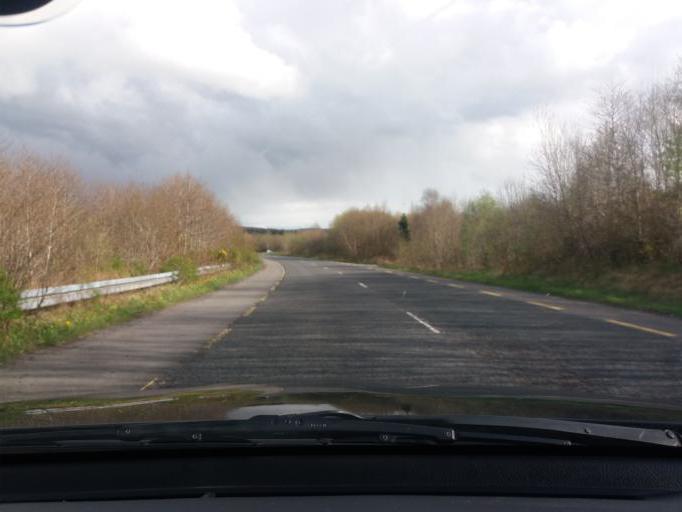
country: IE
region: Connaught
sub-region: County Leitrim
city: Manorhamilton
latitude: 54.3233
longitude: -8.2056
